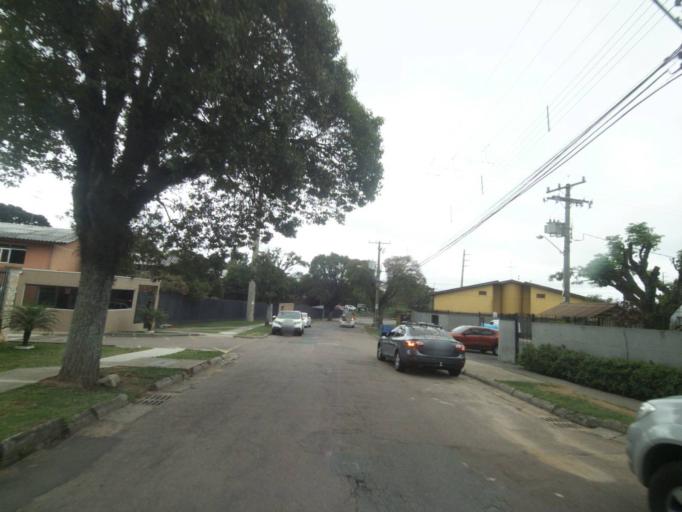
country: BR
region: Parana
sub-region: Sao Jose Dos Pinhais
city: Sao Jose dos Pinhais
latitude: -25.5367
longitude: -49.2843
